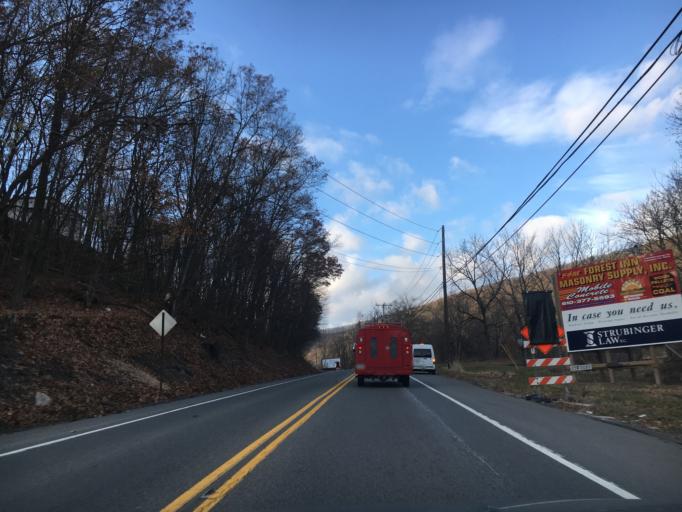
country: US
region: Pennsylvania
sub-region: Carbon County
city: Lehighton
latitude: 40.8569
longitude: -75.7168
